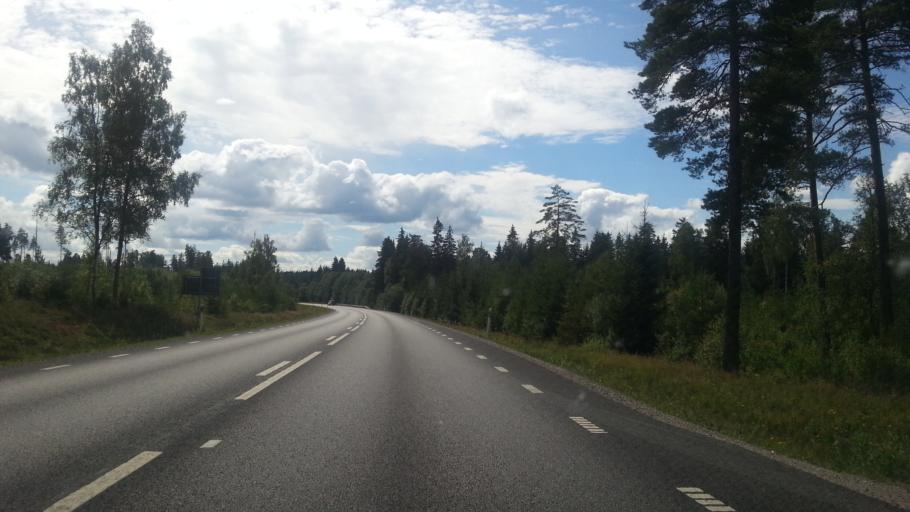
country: SE
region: OErebro
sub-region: Lindesbergs Kommun
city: Lindesberg
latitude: 59.6122
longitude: 15.1849
